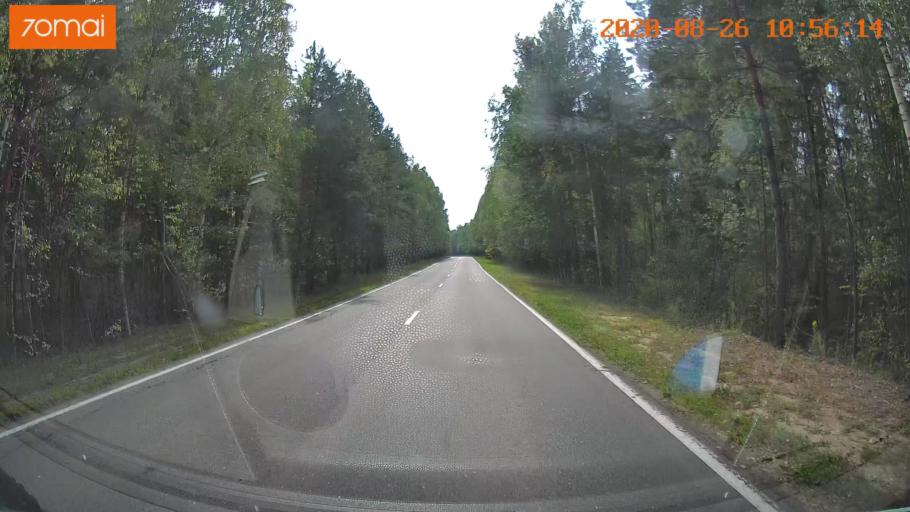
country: RU
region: Rjazan
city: Izhevskoye
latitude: 54.6060
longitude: 41.1852
